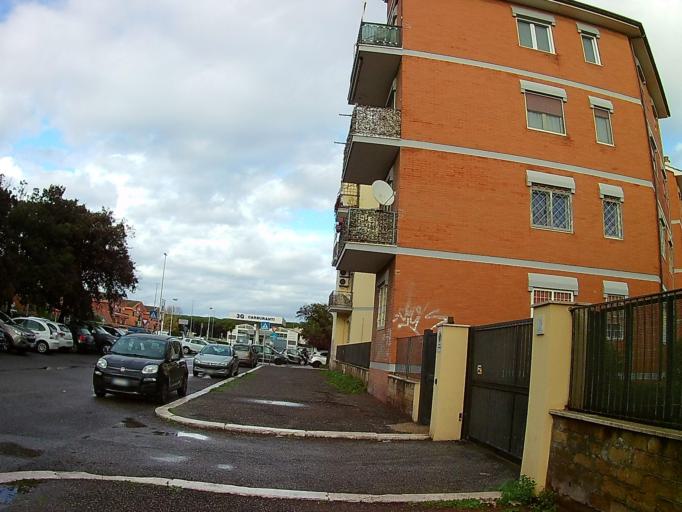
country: IT
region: Latium
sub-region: Citta metropolitana di Roma Capitale
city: Lido di Ostia
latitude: 41.7368
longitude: 12.2926
